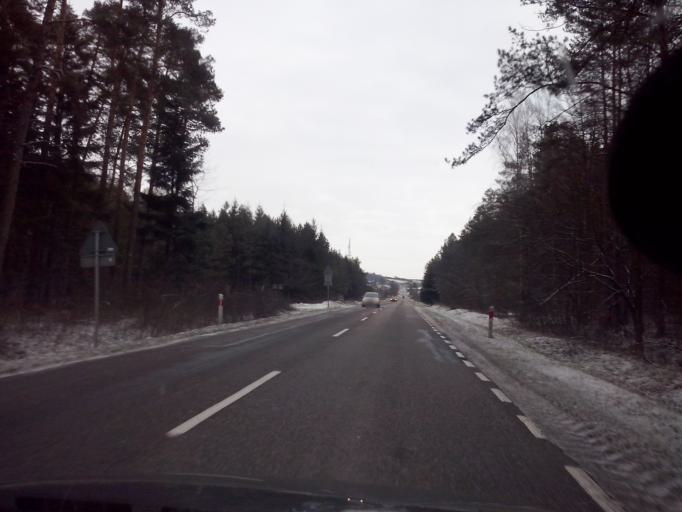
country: PL
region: Lublin Voivodeship
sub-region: Powiat bilgorajski
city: Tereszpol
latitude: 50.5981
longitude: 22.8691
